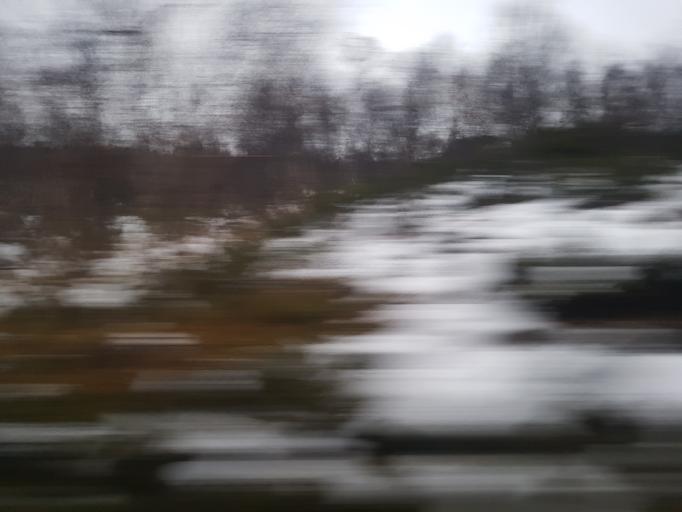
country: NO
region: Sor-Trondelag
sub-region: Oppdal
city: Oppdal
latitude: 62.3043
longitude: 9.6050
